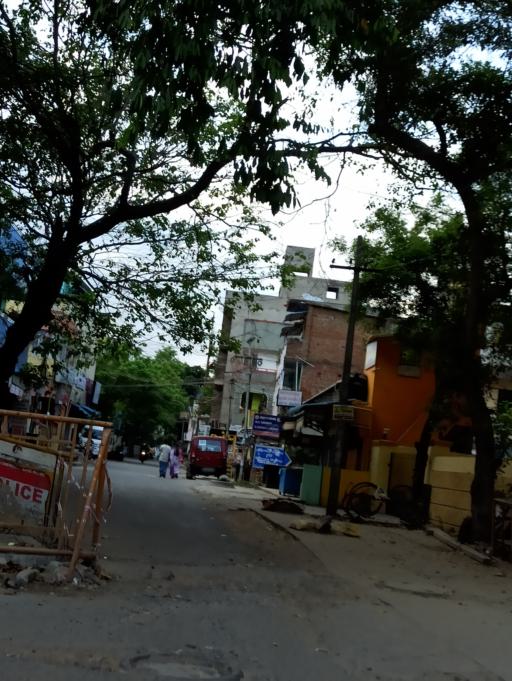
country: IN
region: Tamil Nadu
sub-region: Chennai
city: Chetput
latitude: 13.0538
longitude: 80.2077
